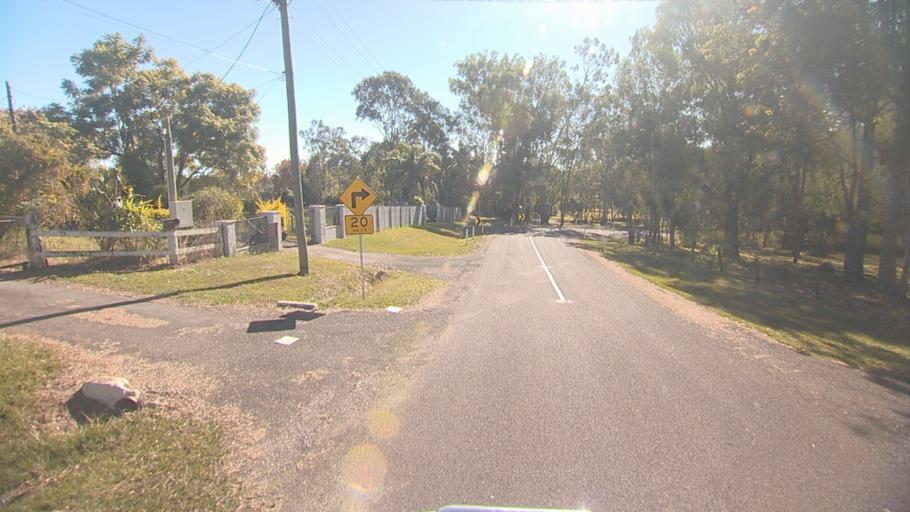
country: AU
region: Queensland
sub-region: Logan
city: Chambers Flat
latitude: -27.7548
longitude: 153.0698
